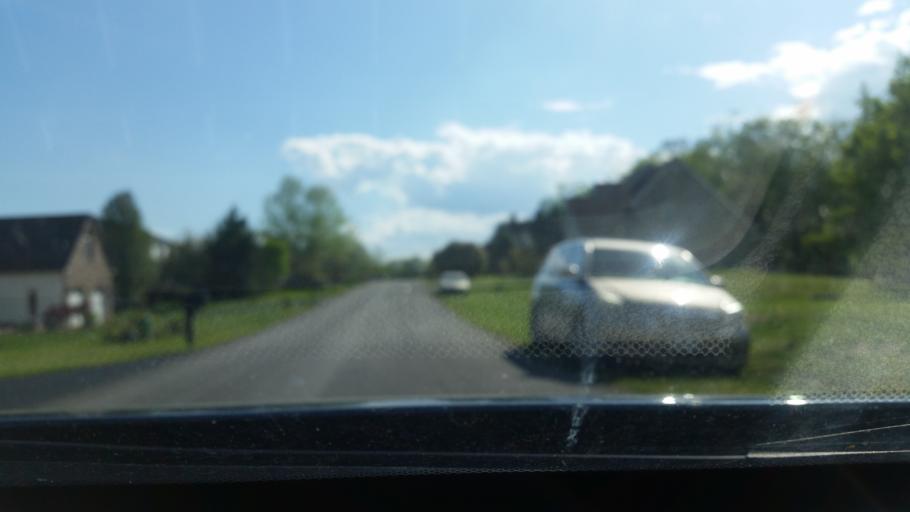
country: US
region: Virginia
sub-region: Giles County
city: Pembroke
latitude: 37.3095
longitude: -80.6297
